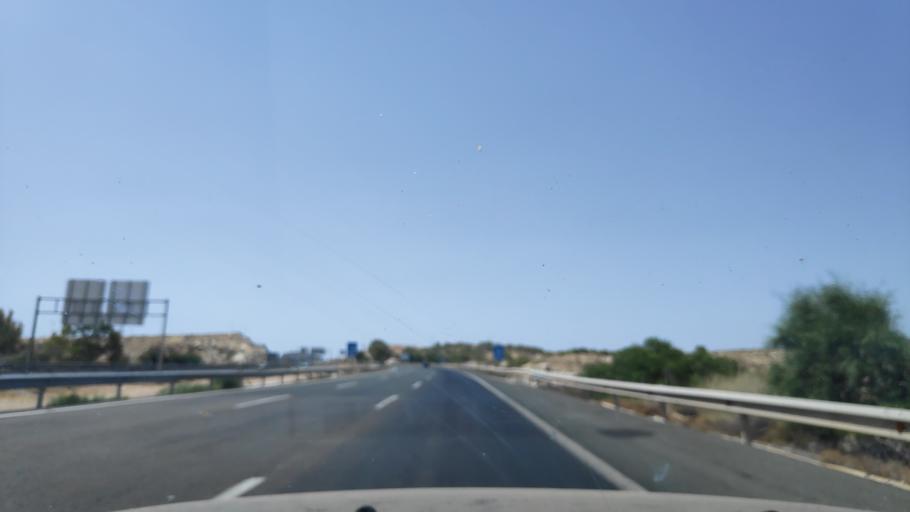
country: ES
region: Murcia
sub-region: Murcia
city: Murcia
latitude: 37.8775
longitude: -1.1300
